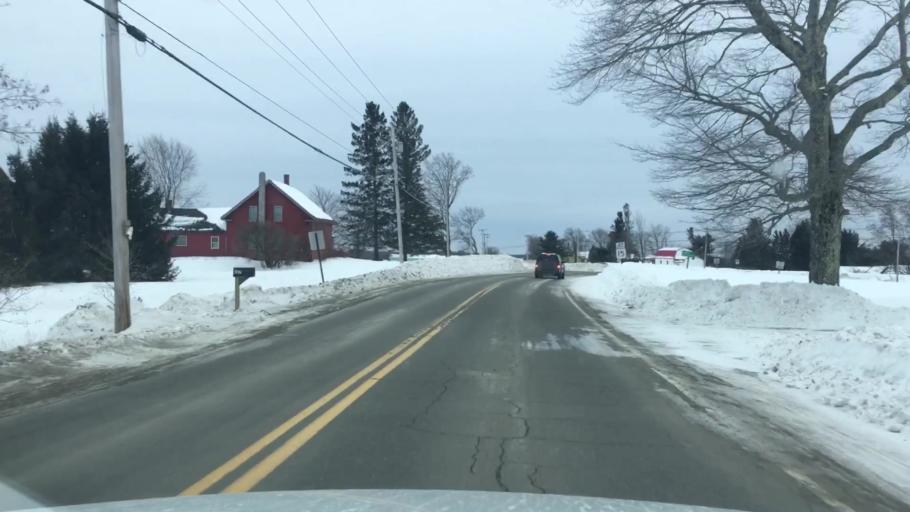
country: US
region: Maine
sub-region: Penobscot County
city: Charleston
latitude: 45.0305
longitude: -69.0313
